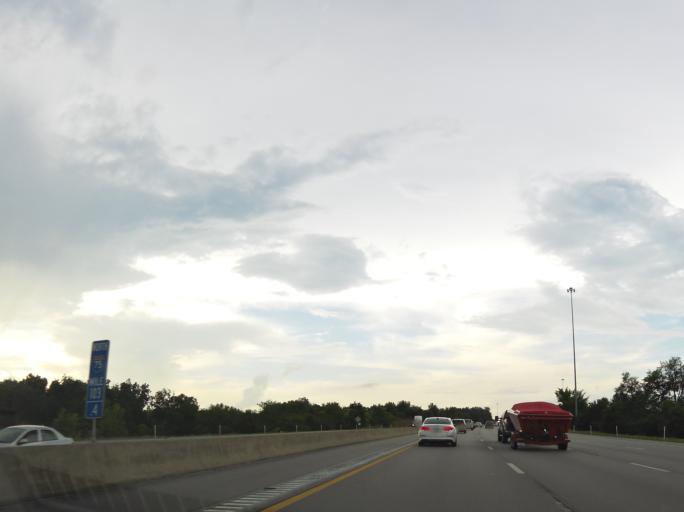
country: US
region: Kentucky
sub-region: Fayette County
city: Lexington
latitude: 37.9549
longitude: -84.3882
